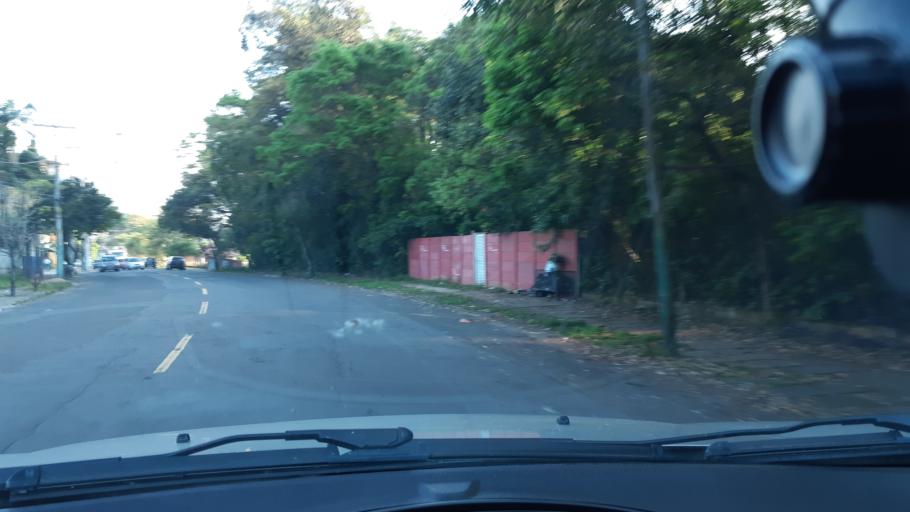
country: BR
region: Rio Grande do Sul
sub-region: Sao Leopoldo
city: Sao Leopoldo
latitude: -29.7705
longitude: -51.1361
